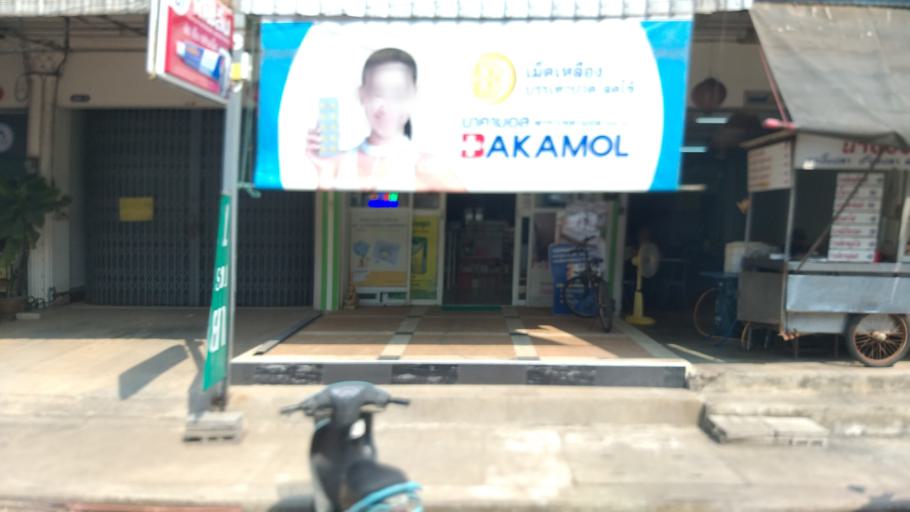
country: TH
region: Changwat Udon Thani
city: Udon Thani
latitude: 17.4180
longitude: 102.7724
